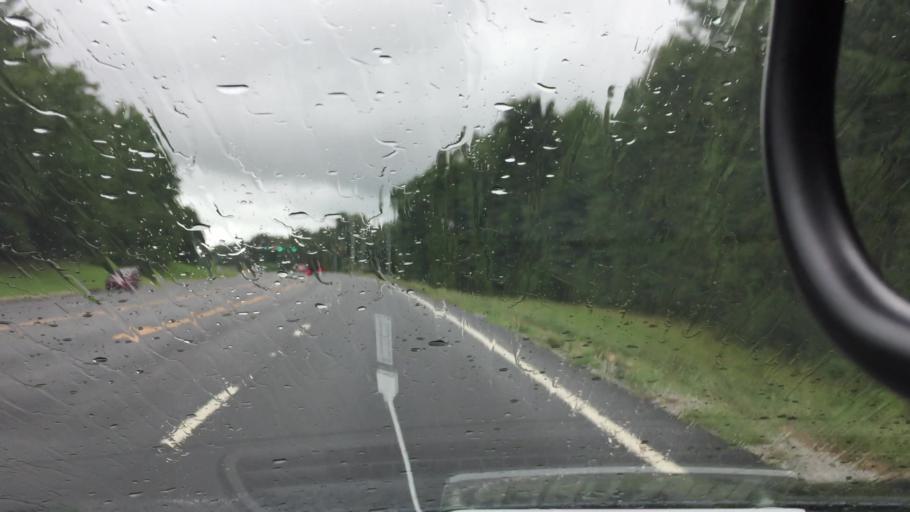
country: US
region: Alabama
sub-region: Lee County
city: Opelika
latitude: 32.6538
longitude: -85.3560
